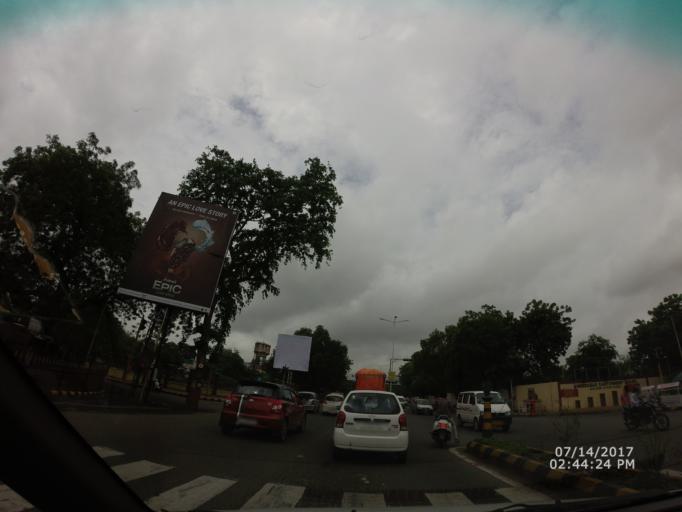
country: IN
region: Gujarat
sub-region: Ahmadabad
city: Ahmedabad
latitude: 23.0714
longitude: 72.6033
